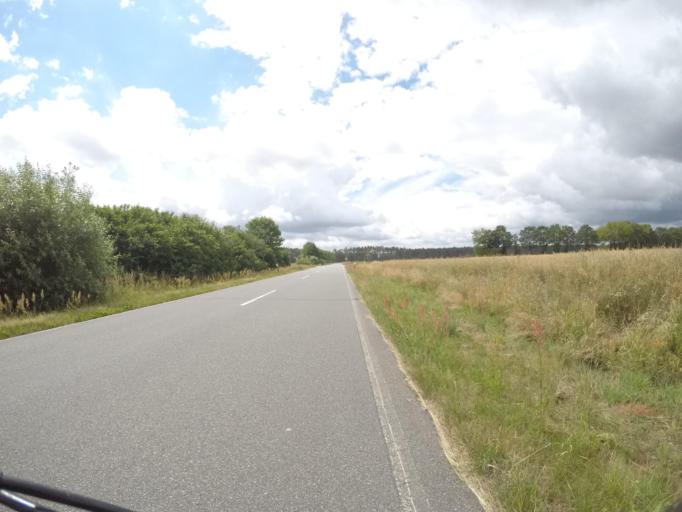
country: DE
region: Lower Saxony
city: Hitzacker
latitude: 53.1983
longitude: 11.1089
